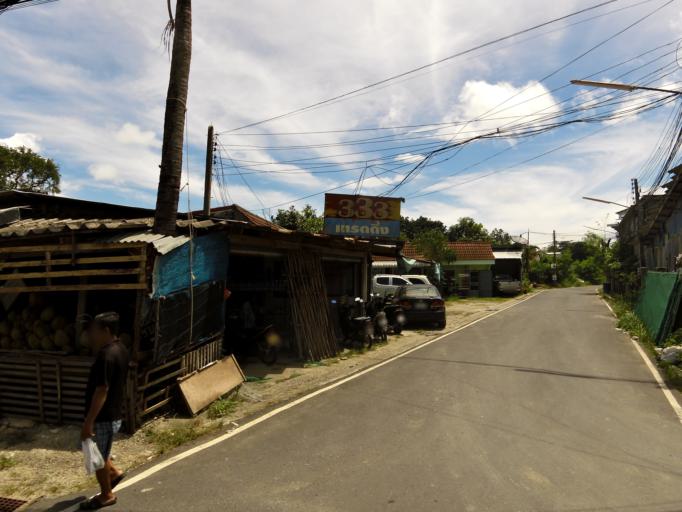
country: TH
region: Phuket
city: Mueang Phuket
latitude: 7.8672
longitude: 98.3527
